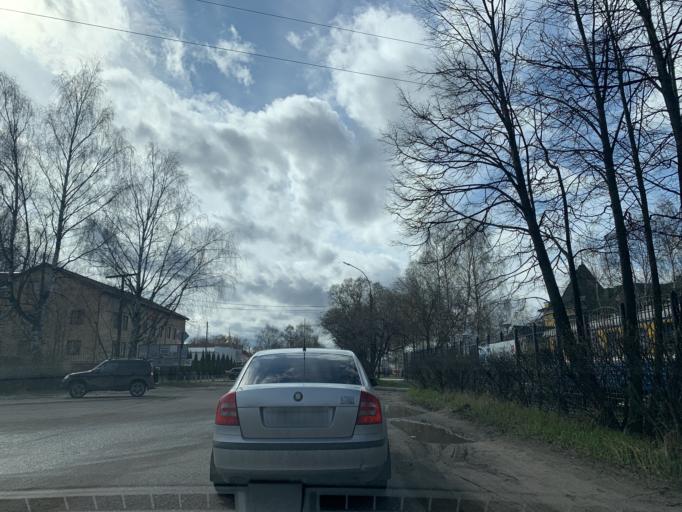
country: RU
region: Jaroslavl
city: Yaroslavl
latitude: 57.6594
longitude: 39.9624
